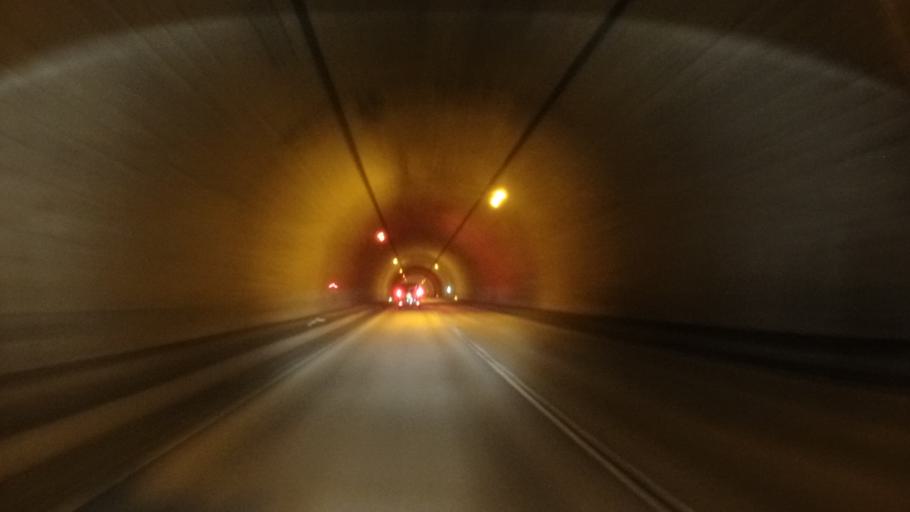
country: JP
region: Ishikawa
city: Nanao
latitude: 37.3348
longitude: 136.8226
